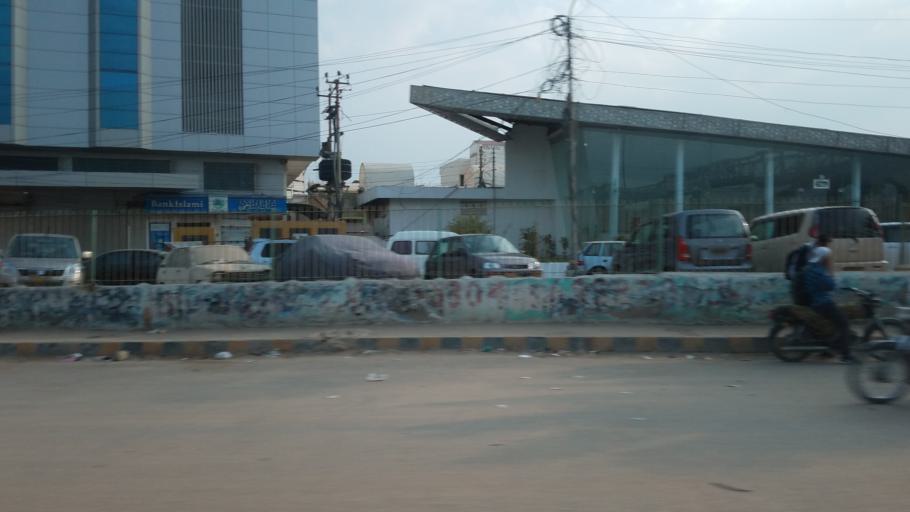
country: PK
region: Sindh
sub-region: Karachi District
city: Karachi
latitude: 24.9306
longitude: 67.0868
